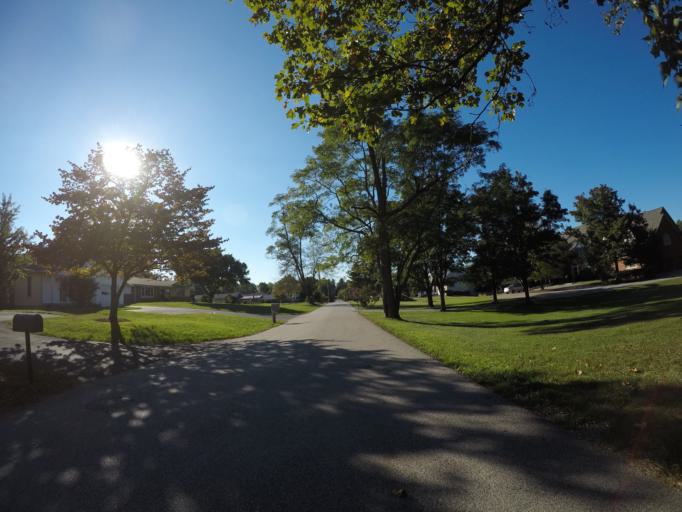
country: US
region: Maryland
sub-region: Howard County
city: Ellicott City
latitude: 39.2948
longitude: -76.7980
